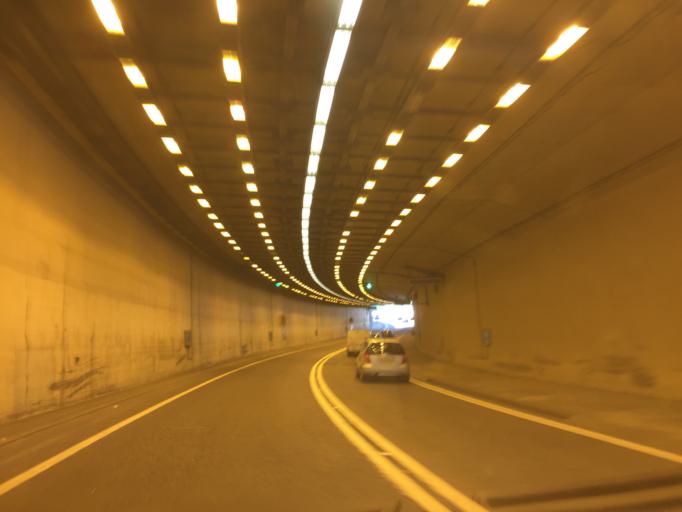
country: GB
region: England
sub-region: Greater London
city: Woodford Green
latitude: 51.5718
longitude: 0.0174
